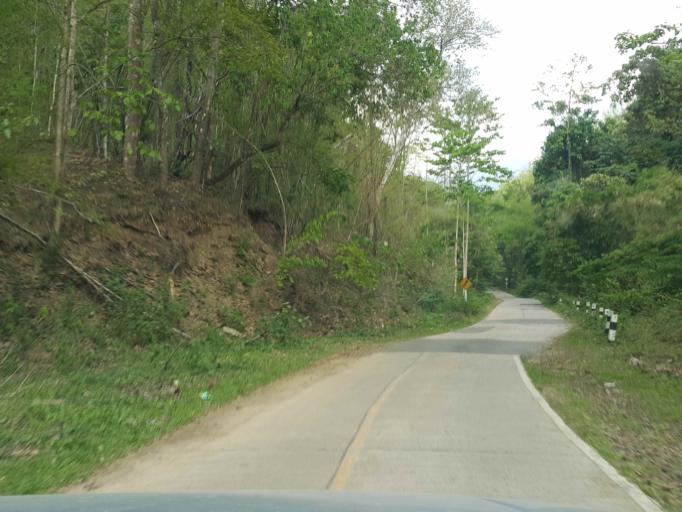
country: TH
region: Chiang Mai
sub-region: Amphoe Chiang Dao
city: Chiang Dao
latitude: 19.4121
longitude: 98.7967
